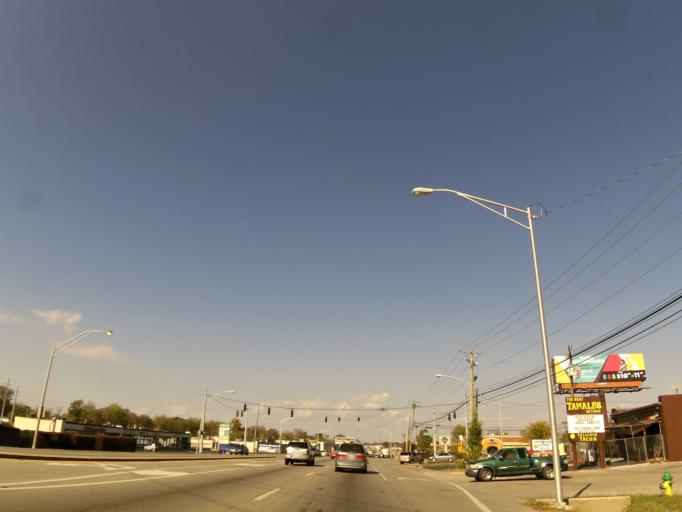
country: US
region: Kentucky
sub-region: Fayette County
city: Lexington-Fayette
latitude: 38.0354
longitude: -84.4539
